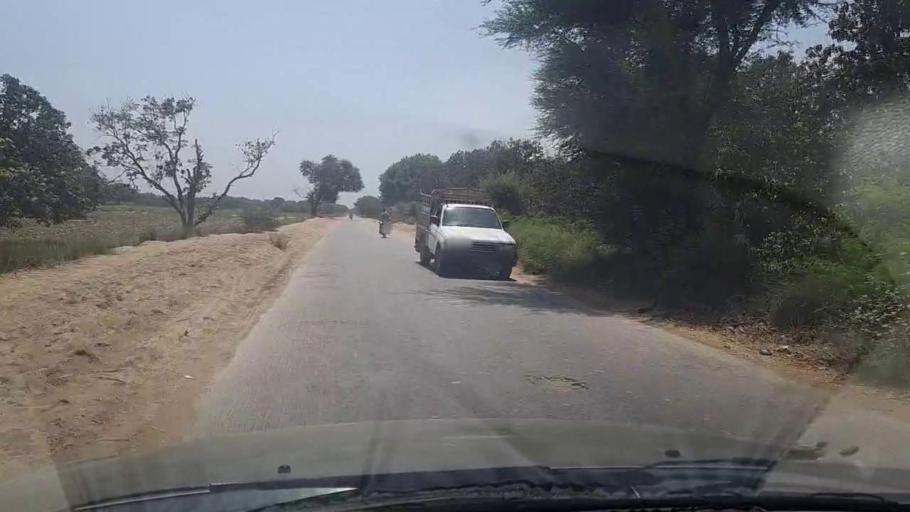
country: PK
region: Sindh
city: Tando Jam
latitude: 25.2973
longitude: 68.5861
